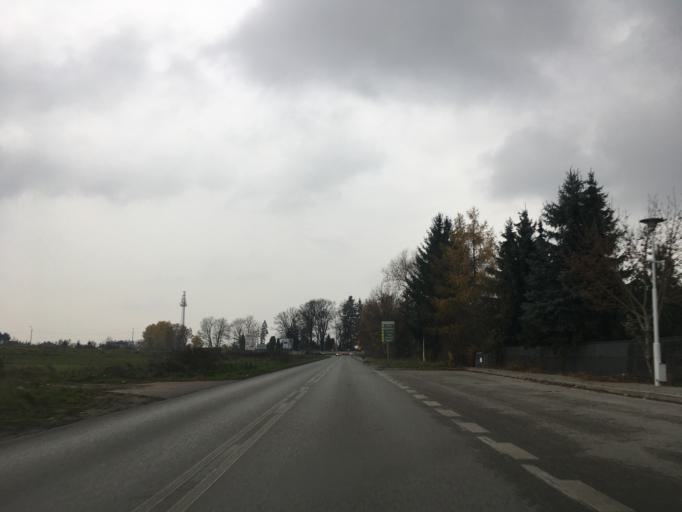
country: PL
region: Masovian Voivodeship
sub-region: Powiat piaseczynski
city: Zalesie Gorne
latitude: 52.0428
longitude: 21.0031
